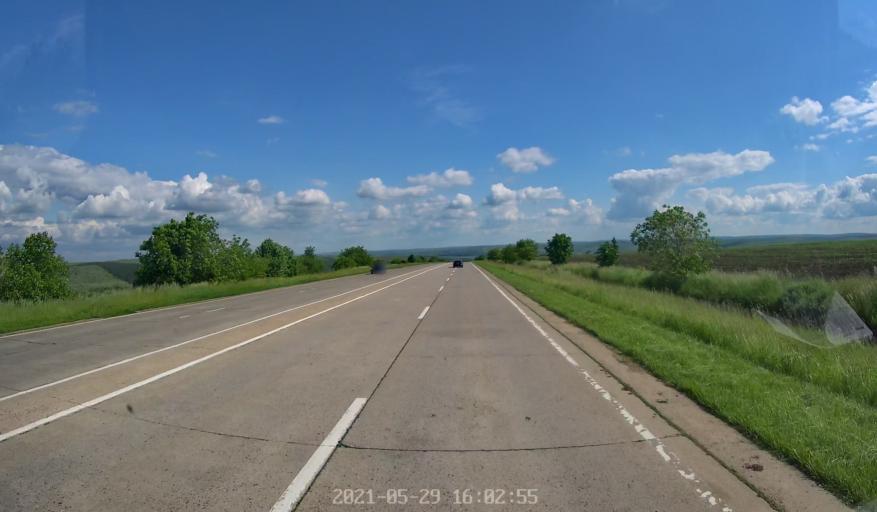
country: MD
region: Chisinau
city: Singera
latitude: 46.8450
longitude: 28.9002
